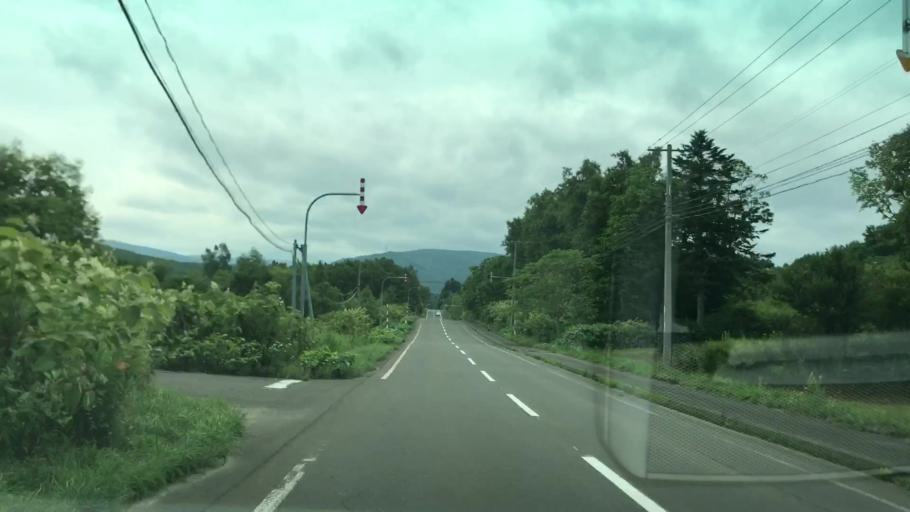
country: JP
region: Hokkaido
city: Yoichi
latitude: 43.0717
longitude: 140.8170
